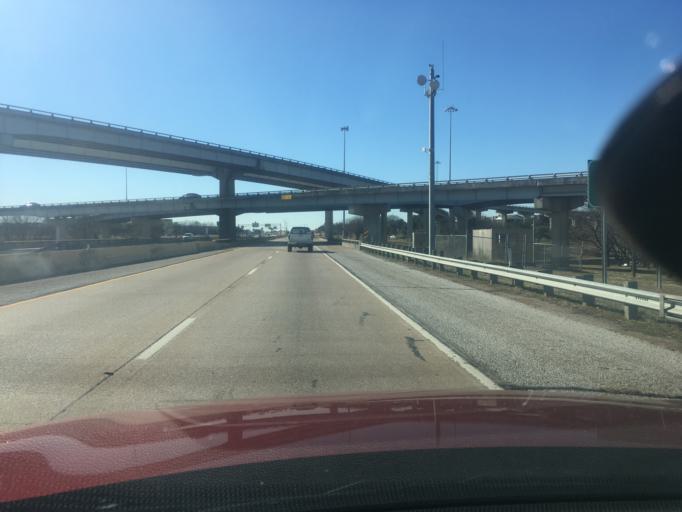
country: US
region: Texas
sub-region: Dallas County
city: Duncanville
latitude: 32.6549
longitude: -96.8771
